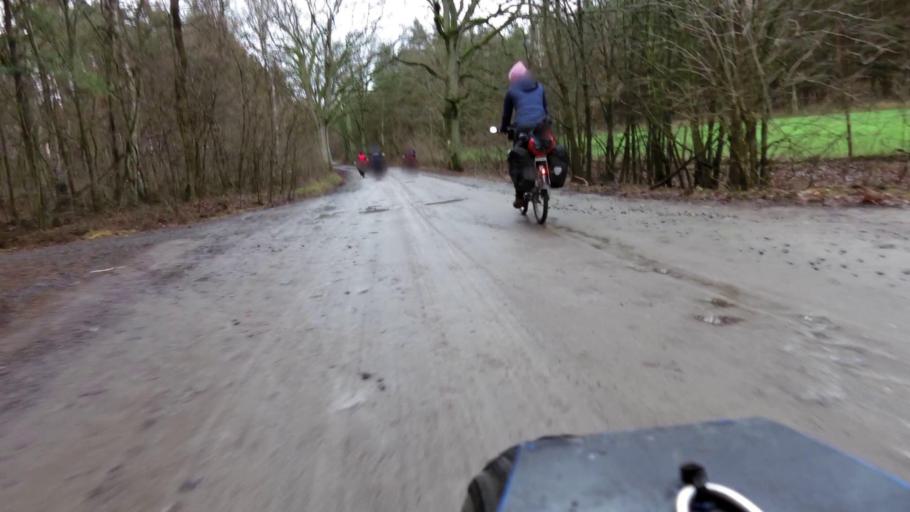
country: PL
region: Lubusz
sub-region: Powiat gorzowski
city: Witnica
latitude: 52.6926
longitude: 14.8526
